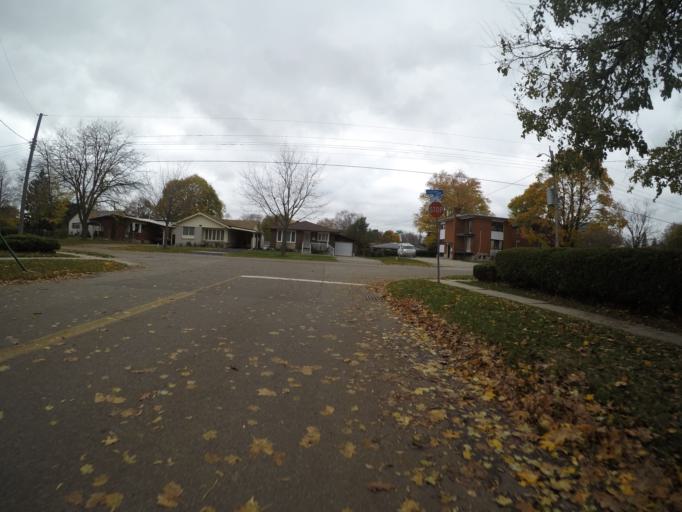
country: CA
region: Ontario
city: Kitchener
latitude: 43.4285
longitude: -80.4546
